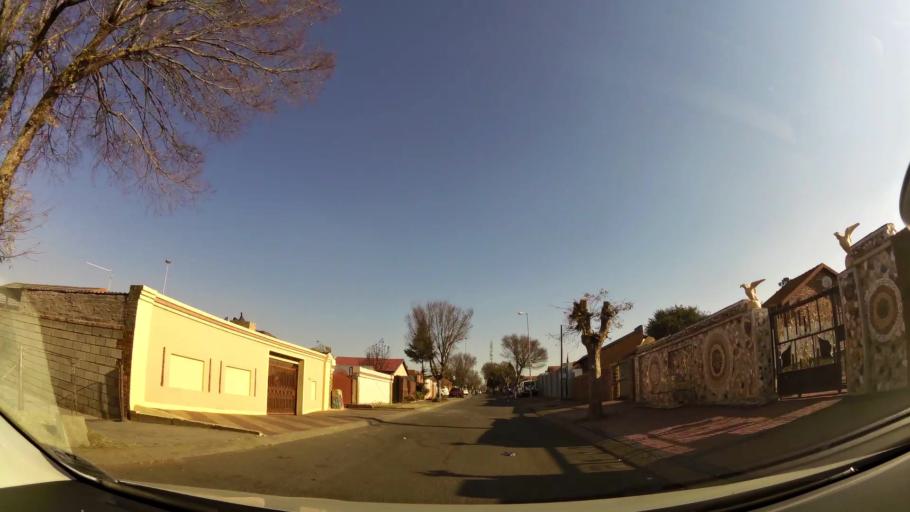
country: ZA
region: Gauteng
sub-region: City of Johannesburg Metropolitan Municipality
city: Soweto
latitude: -26.2668
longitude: 27.8782
